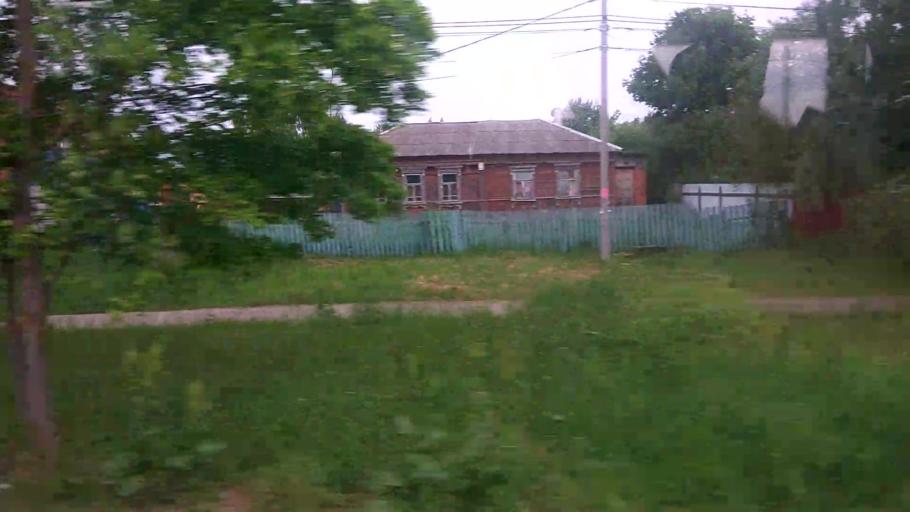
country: RU
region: Moskovskaya
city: Lukhovitsy
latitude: 54.9402
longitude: 39.0161
